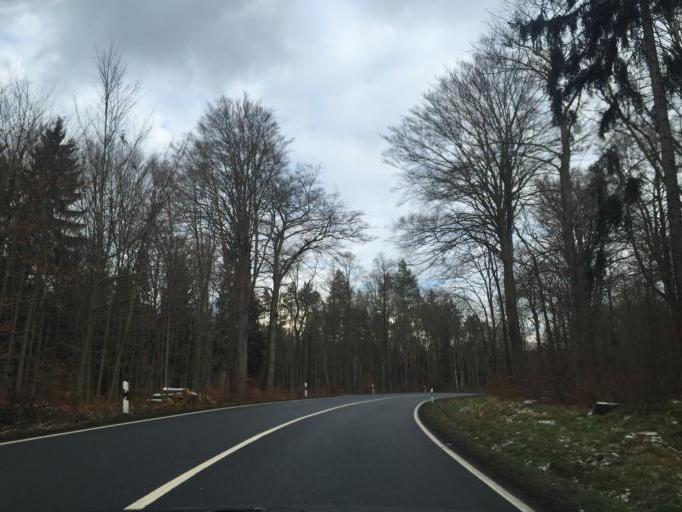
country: DE
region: Saxony
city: Radeberg
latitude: 51.0971
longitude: 13.8512
